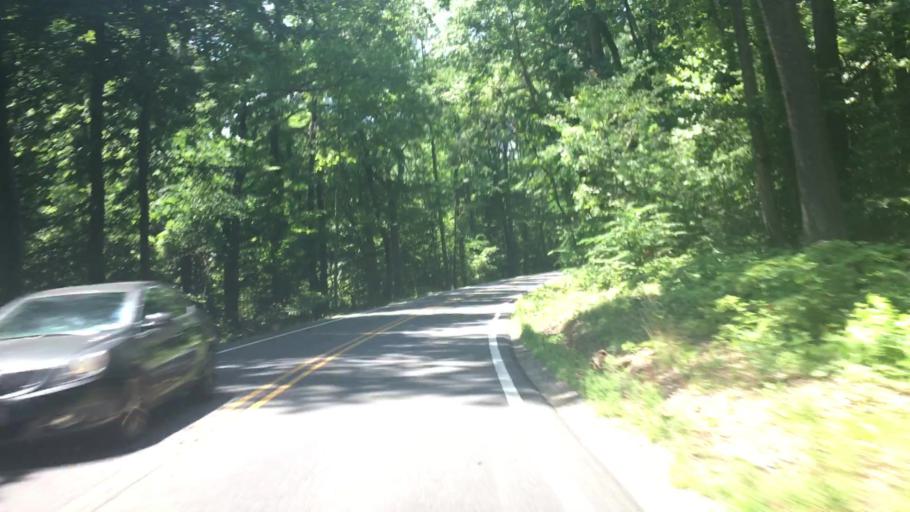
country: US
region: Virginia
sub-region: King George County
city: King George
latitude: 38.3231
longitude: -77.1692
